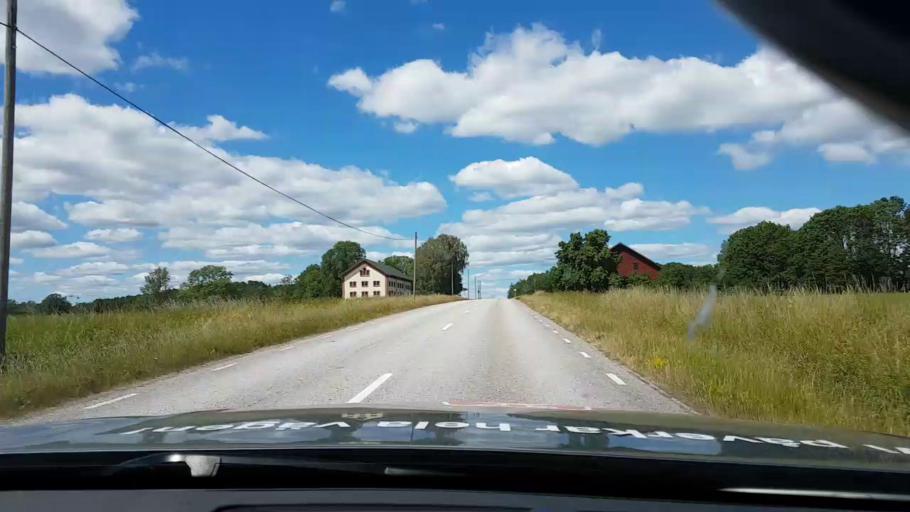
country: SE
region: Kalmar
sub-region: Vasterviks Kommun
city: Forserum
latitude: 58.0454
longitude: 16.4157
